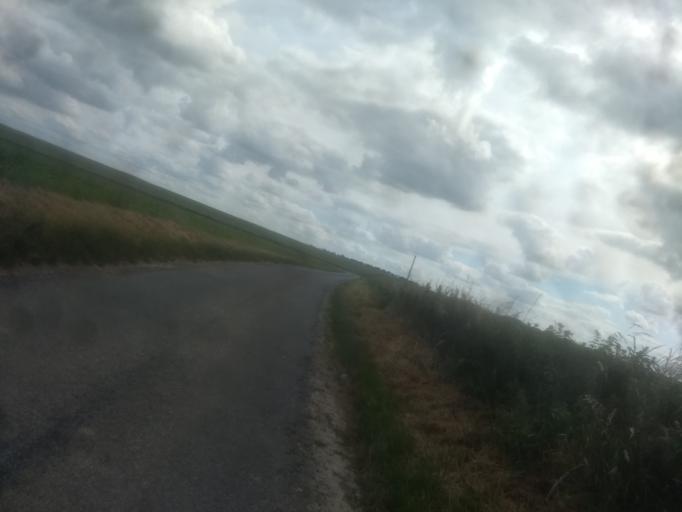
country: FR
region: Nord-Pas-de-Calais
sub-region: Departement du Pas-de-Calais
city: Duisans
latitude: 50.2926
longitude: 2.6924
